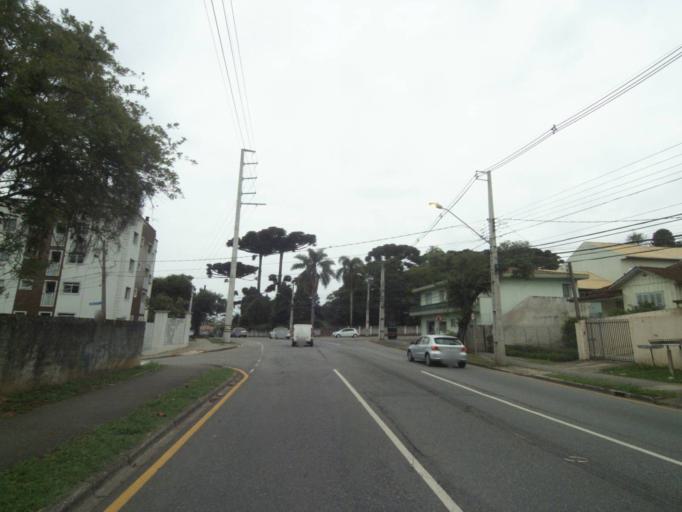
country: BR
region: Parana
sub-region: Curitiba
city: Curitiba
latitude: -25.4018
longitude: -49.2752
